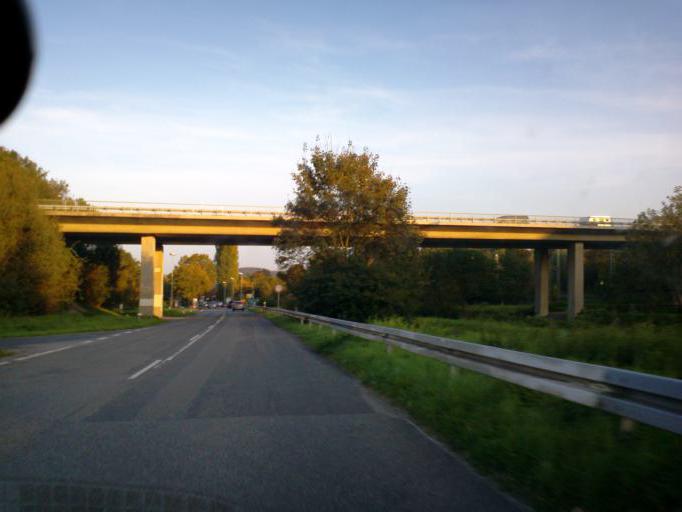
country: DE
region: Baden-Wuerttemberg
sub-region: Karlsruhe Region
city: Weingarten
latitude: 49.0086
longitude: 8.4869
